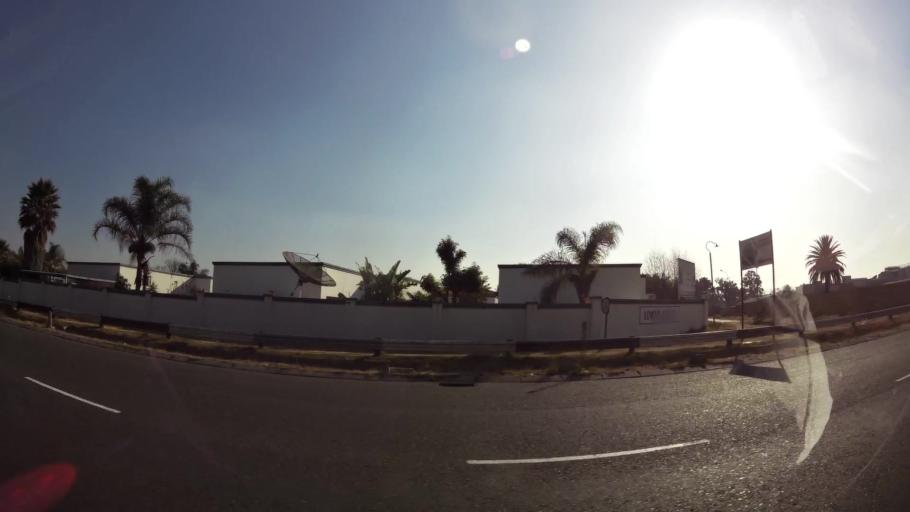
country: ZA
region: Gauteng
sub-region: West Rand District Municipality
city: Randfontein
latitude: -26.1673
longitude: 27.7120
